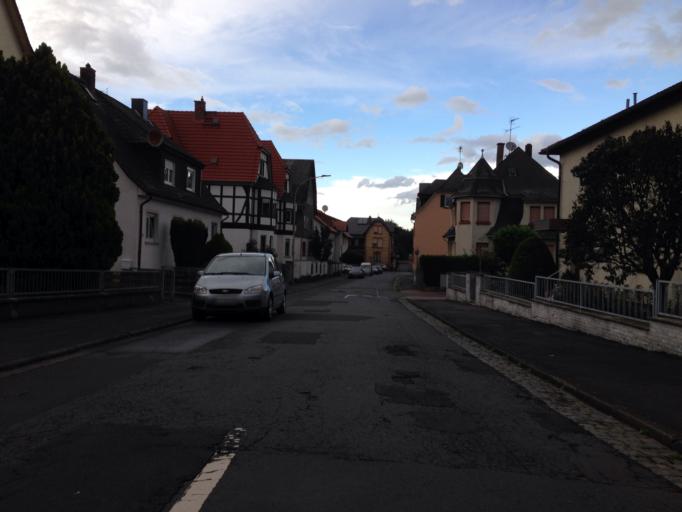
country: DE
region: Hesse
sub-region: Regierungsbezirk Giessen
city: Hungen
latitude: 50.4753
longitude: 8.8920
